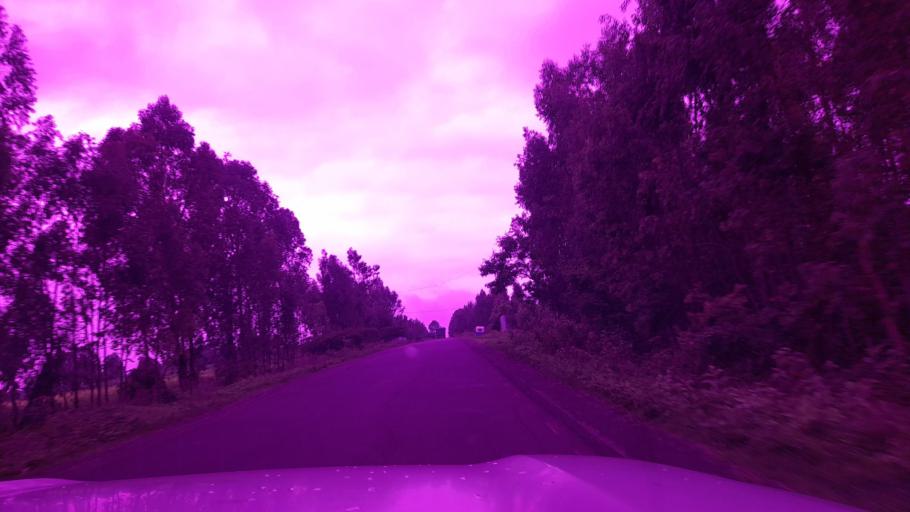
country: ET
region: Oromiya
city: Waliso
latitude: 8.2624
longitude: 37.6481
